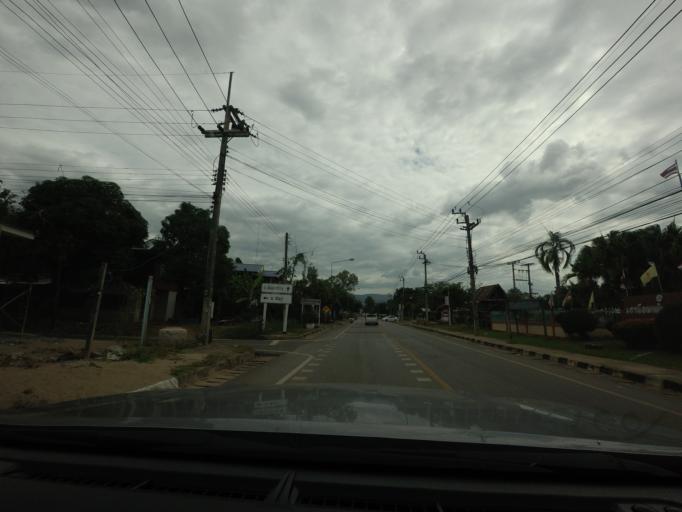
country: TH
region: Phitsanulok
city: Noen Maprang
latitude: 16.6774
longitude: 100.6117
